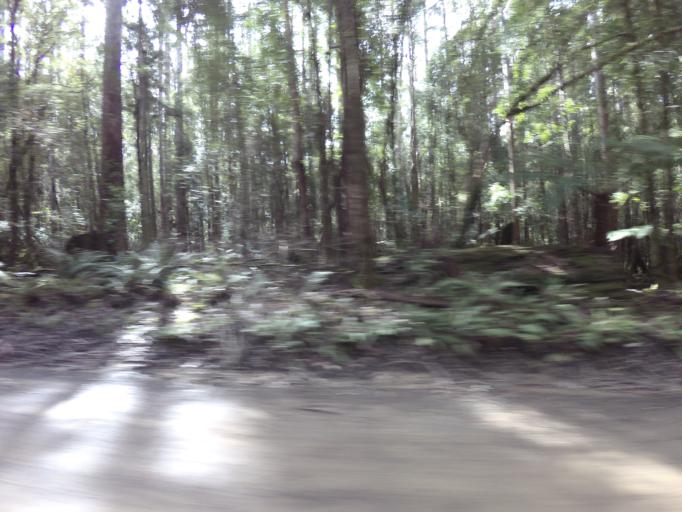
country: AU
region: Tasmania
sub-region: Huon Valley
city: Geeveston
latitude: -43.3838
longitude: 146.8427
